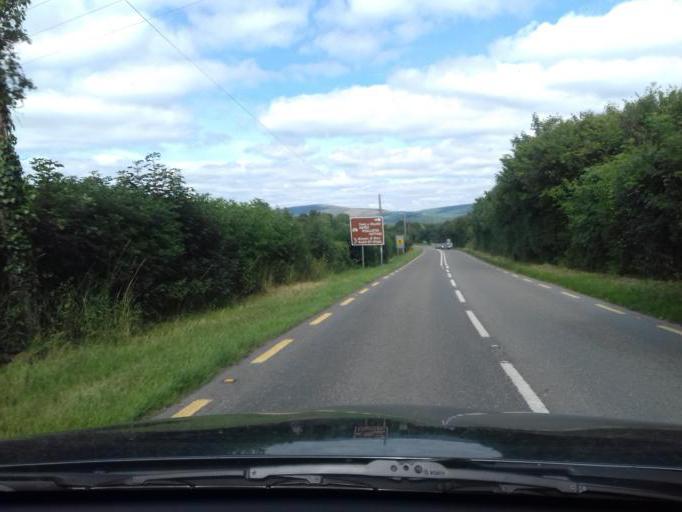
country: IE
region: Leinster
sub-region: Wicklow
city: Baltinglass
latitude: 52.9946
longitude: -6.6505
